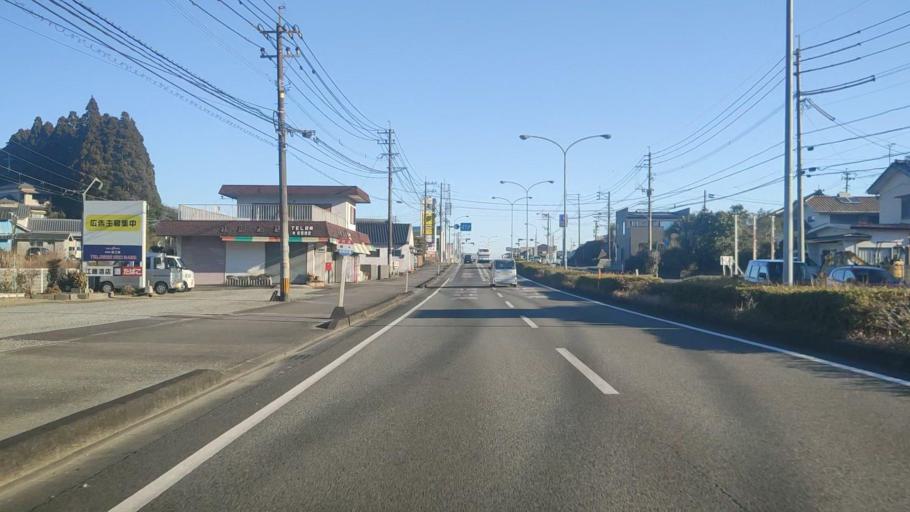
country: JP
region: Miyazaki
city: Nobeoka
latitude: 32.4563
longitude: 131.6442
